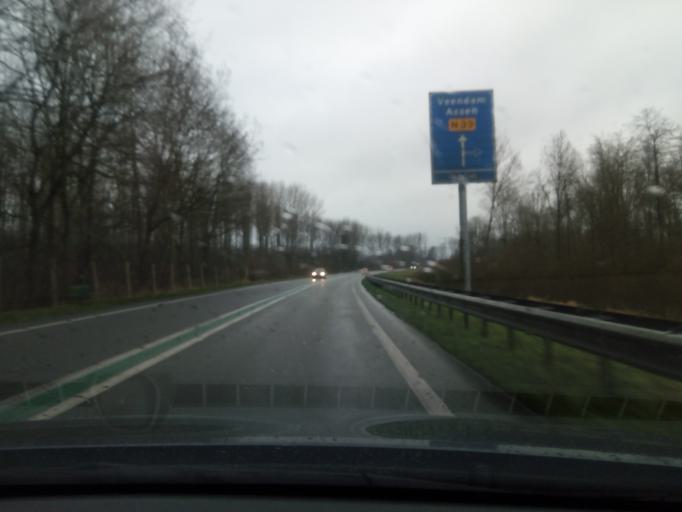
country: NL
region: Groningen
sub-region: Gemeente Appingedam
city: Appingedam
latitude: 53.2737
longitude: 6.8718
